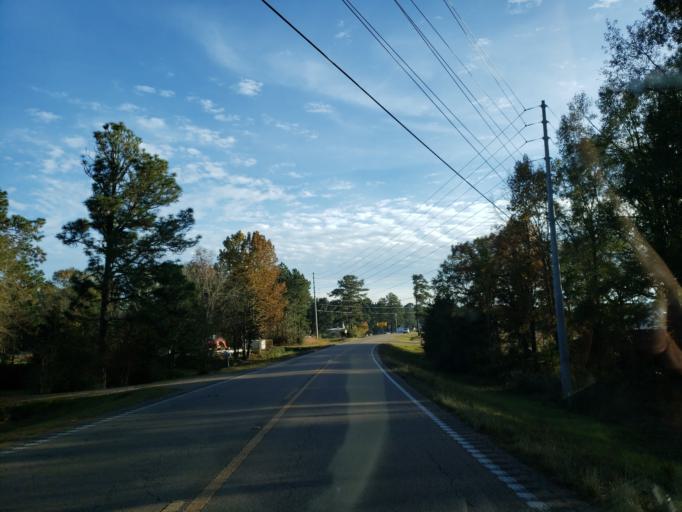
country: US
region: Mississippi
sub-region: Lamar County
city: West Hattiesburg
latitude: 31.3003
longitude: -89.4692
